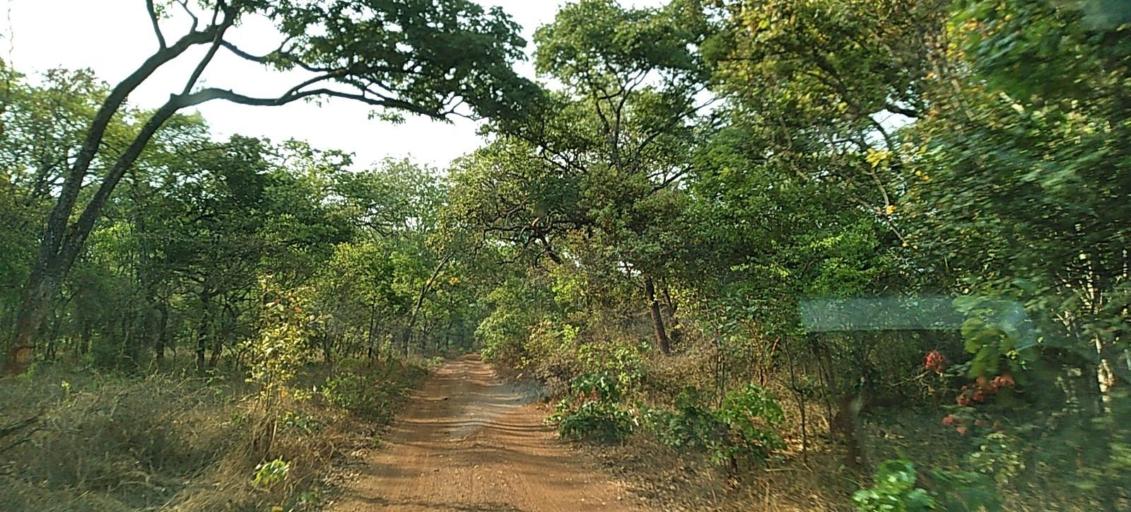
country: ZM
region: Copperbelt
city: Kalulushi
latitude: -12.9786
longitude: 27.7170
